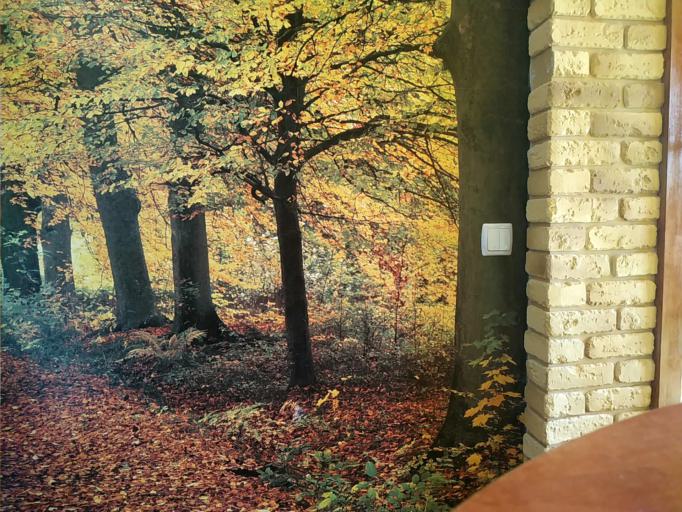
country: RU
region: Jaroslavl
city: Kukoboy
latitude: 58.8936
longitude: 39.6998
